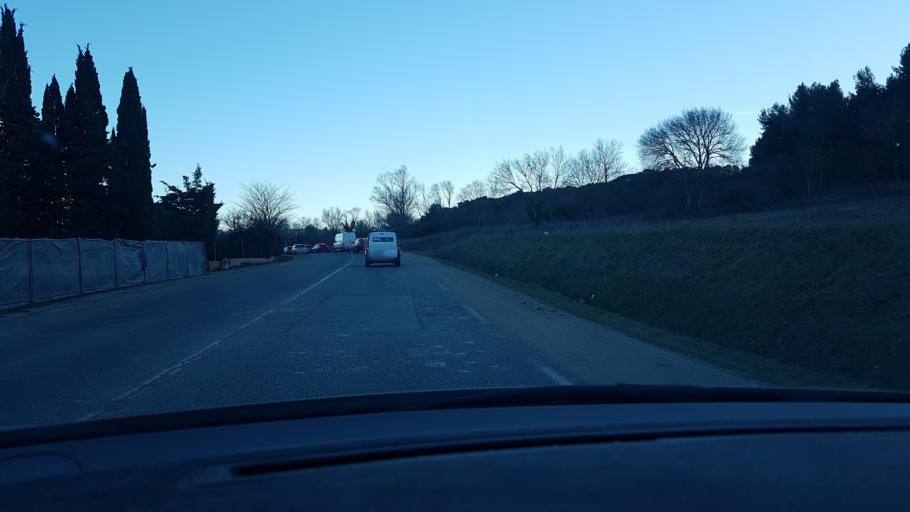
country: FR
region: Provence-Alpes-Cote d'Azur
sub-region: Departement des Bouches-du-Rhone
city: Bouc-Bel-Air
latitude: 43.4964
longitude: 5.4037
